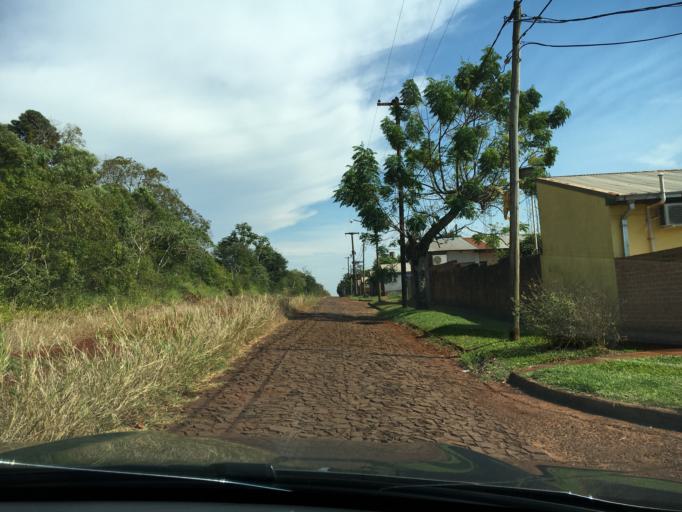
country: AR
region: Misiones
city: Puerto Rico
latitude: -26.8047
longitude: -55.0019
